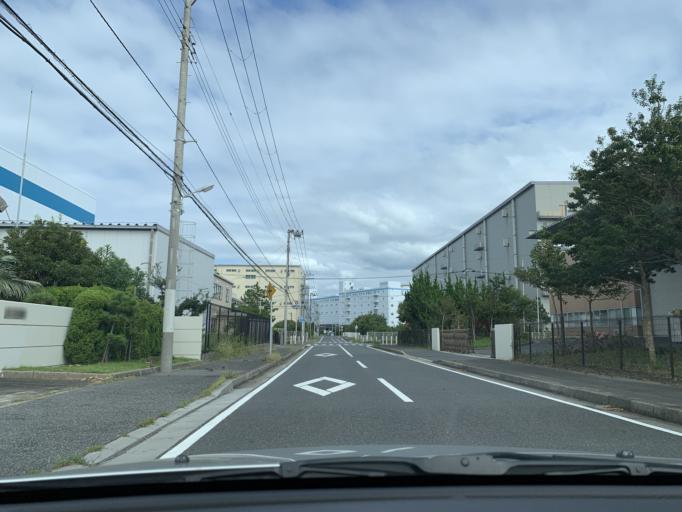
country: JP
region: Tokyo
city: Urayasu
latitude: 35.6212
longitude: 139.8967
